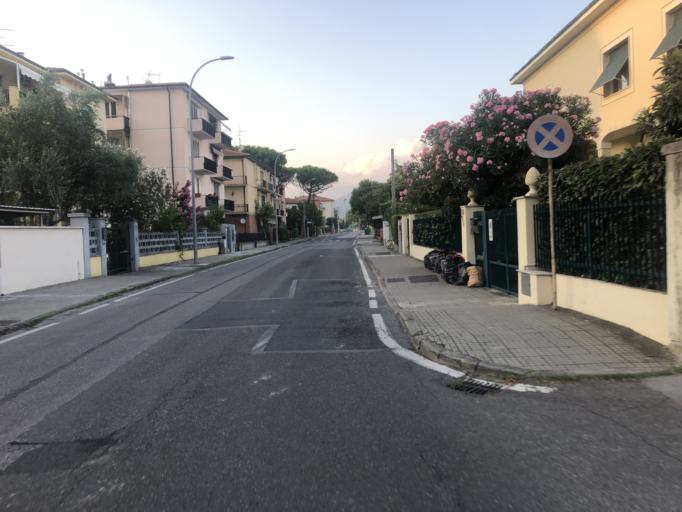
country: IT
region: Tuscany
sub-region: Province of Pisa
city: Pisa
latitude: 43.7310
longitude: 10.4073
